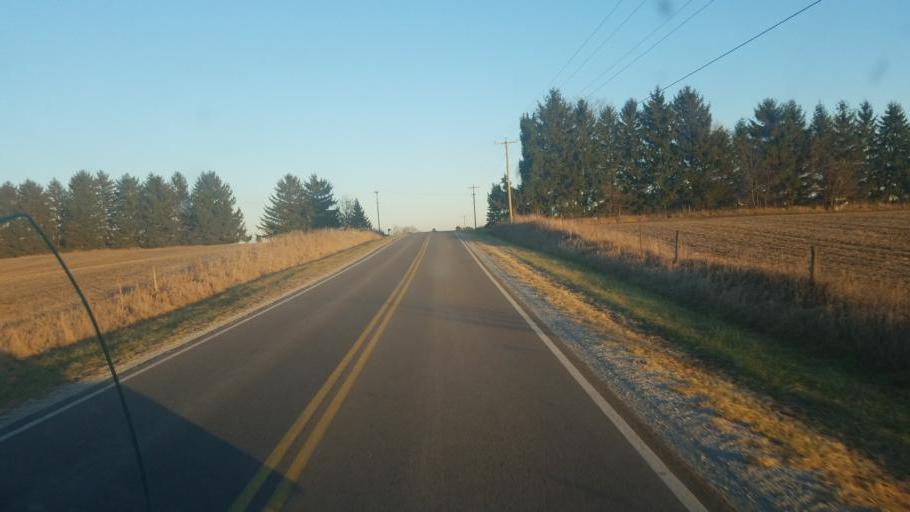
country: US
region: Ohio
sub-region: Hardin County
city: Kenton
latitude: 40.6221
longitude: -83.4327
